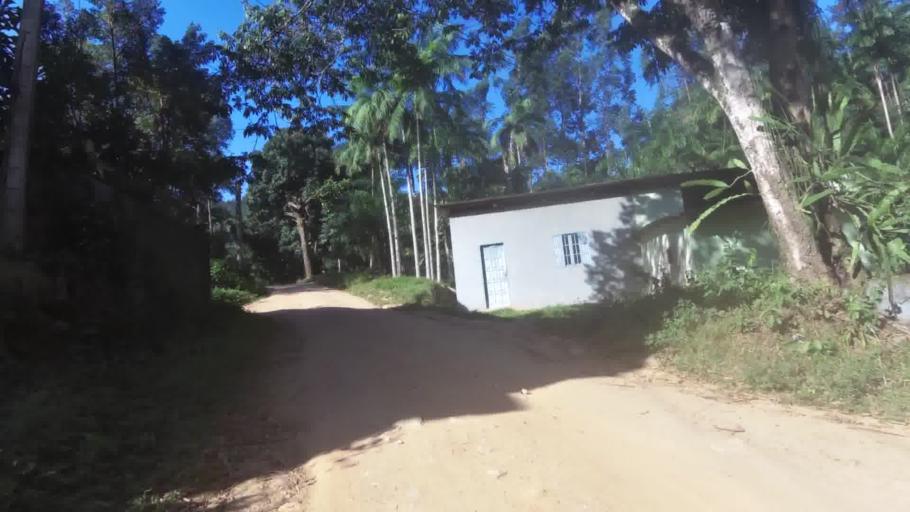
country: BR
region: Espirito Santo
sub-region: Iconha
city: Iconha
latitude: -20.7575
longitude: -40.8174
